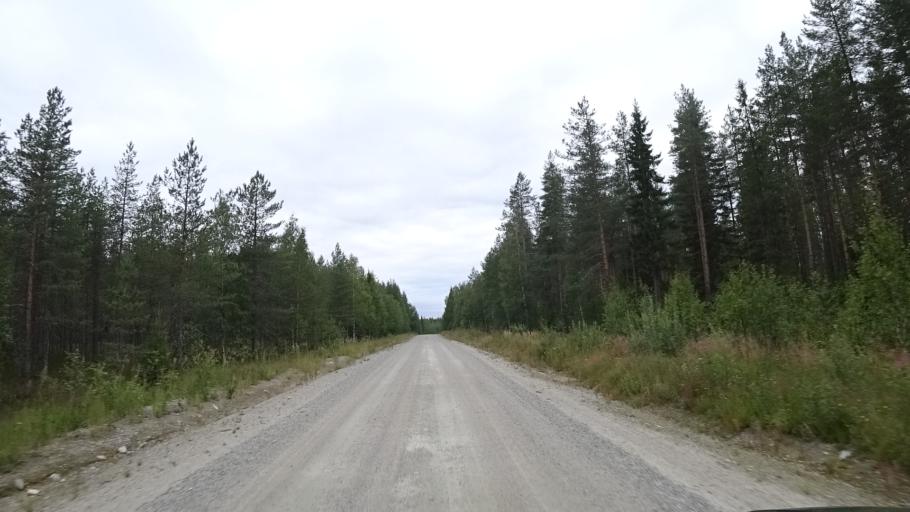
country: FI
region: North Karelia
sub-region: Joensuu
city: Eno
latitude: 63.1562
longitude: 30.5994
